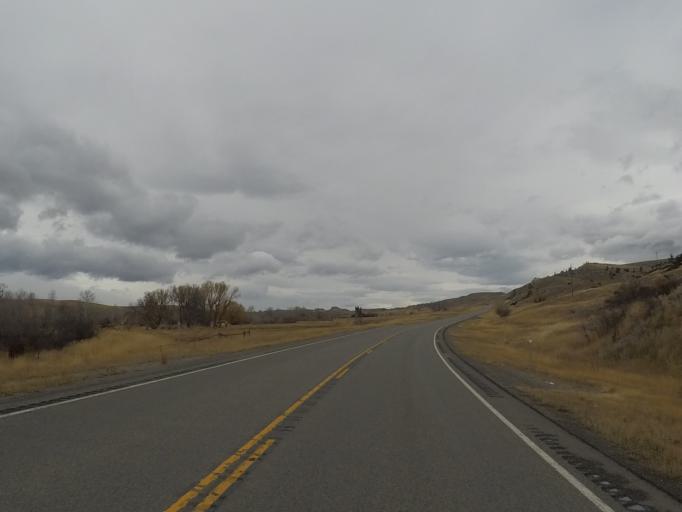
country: US
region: Montana
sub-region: Sweet Grass County
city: Big Timber
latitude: 45.9067
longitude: -109.9782
